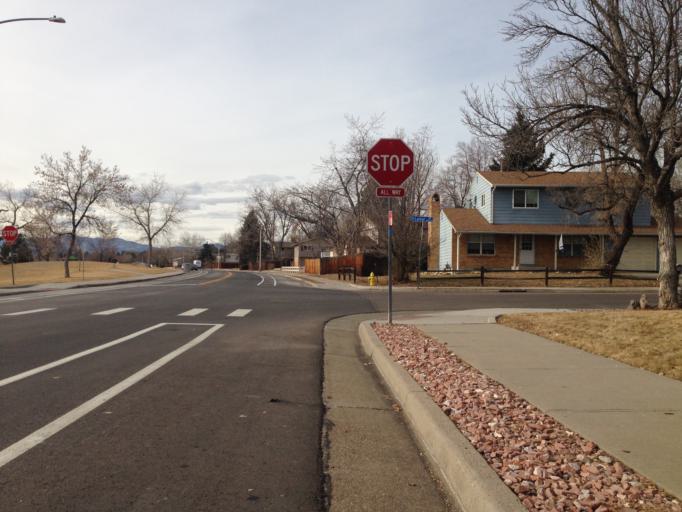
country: US
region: Colorado
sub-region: Adams County
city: Westminster
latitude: 39.8457
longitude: -105.0666
